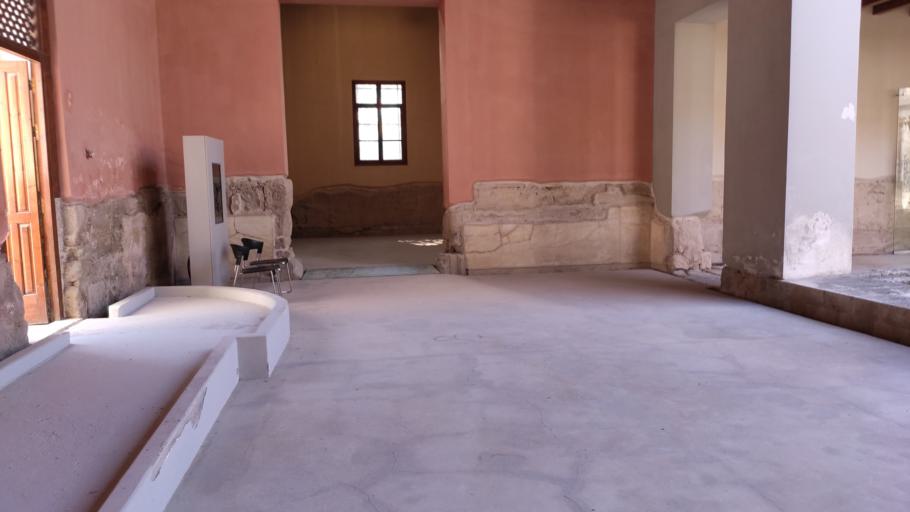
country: GR
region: South Aegean
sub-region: Nomos Dodekanisou
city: Kos
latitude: 36.8897
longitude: 27.2884
